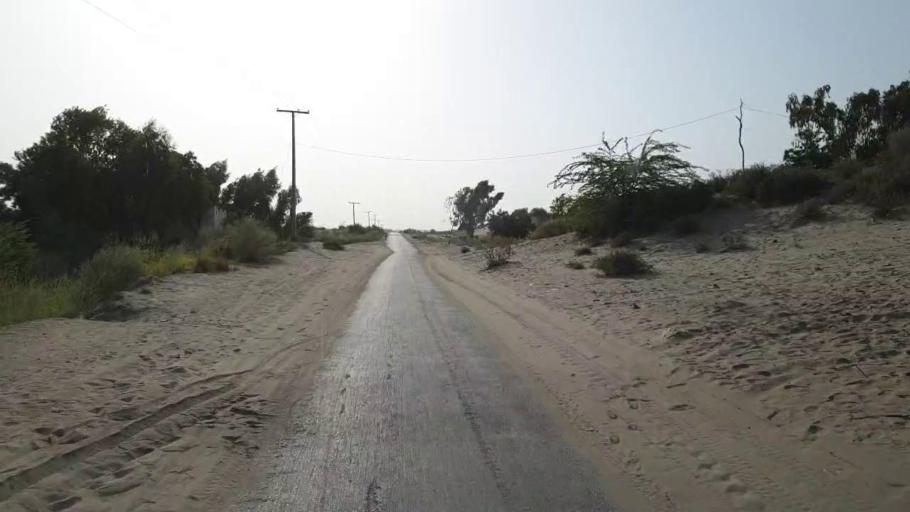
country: PK
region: Sindh
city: Jam Sahib
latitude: 26.4362
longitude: 68.8719
